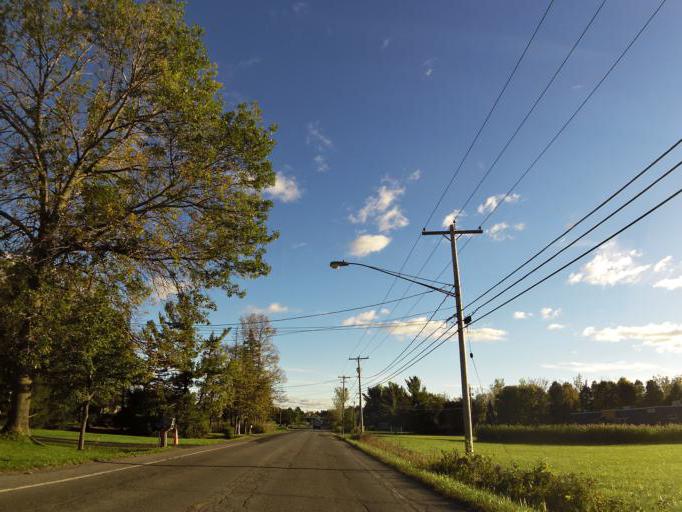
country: US
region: New York
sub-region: Erie County
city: Billington Heights
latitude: 42.8019
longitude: -78.6215
